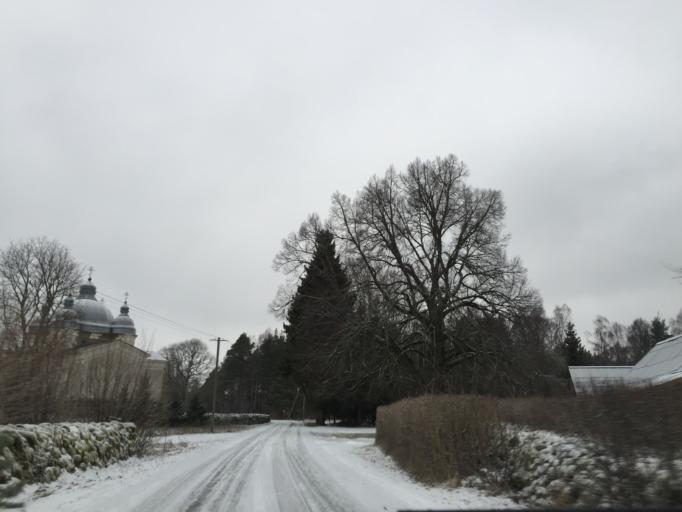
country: EE
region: Saare
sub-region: Orissaare vald
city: Orissaare
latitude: 58.6187
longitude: 23.1864
